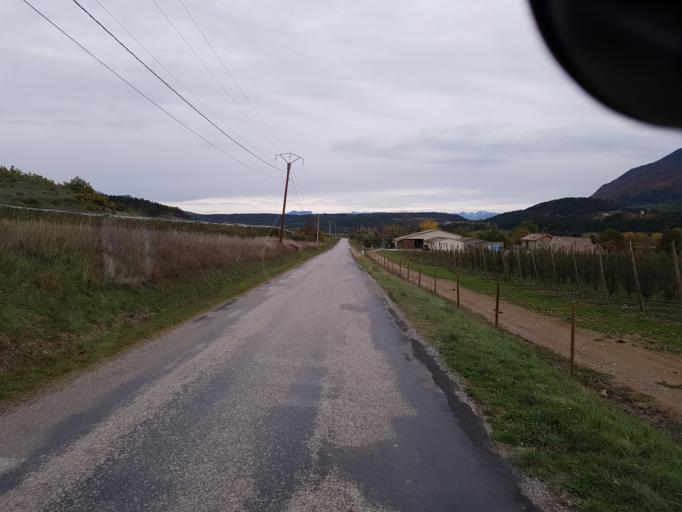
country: FR
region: Provence-Alpes-Cote d'Azur
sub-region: Departement des Hautes-Alpes
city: Laragne-Monteglin
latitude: 44.3199
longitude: 5.7269
